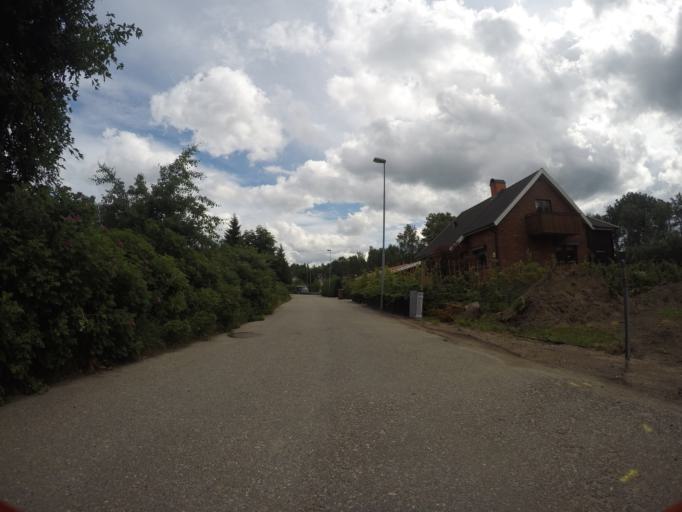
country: SE
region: Vaestra Goetaland
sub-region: Trollhattan
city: Trollhattan
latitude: 58.2267
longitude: 12.3151
